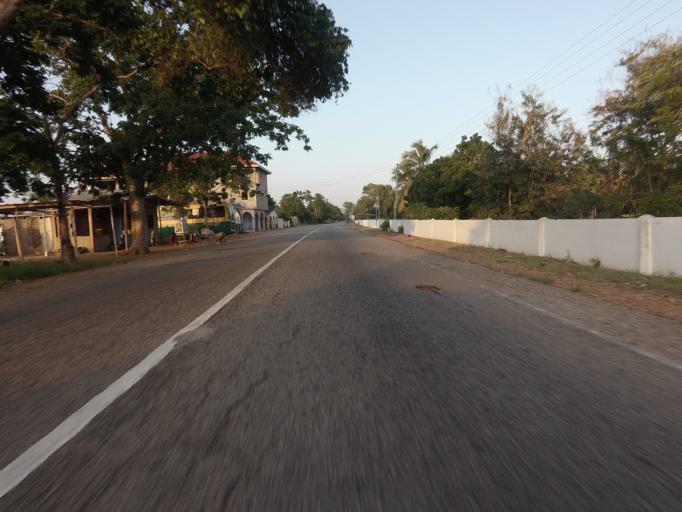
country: GH
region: Volta
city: Anloga
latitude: 5.7900
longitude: 0.8675
